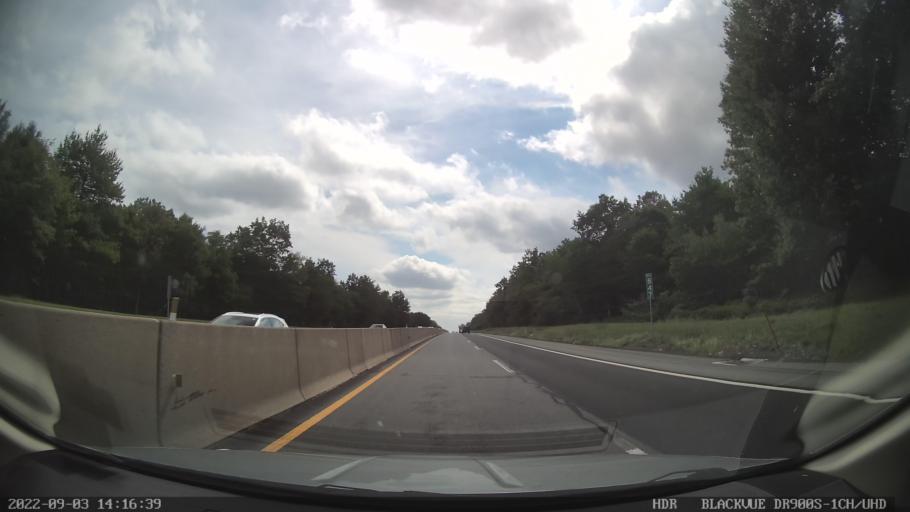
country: US
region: Pennsylvania
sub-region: Carbon County
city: Towamensing Trails
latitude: 40.9502
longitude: -75.6351
